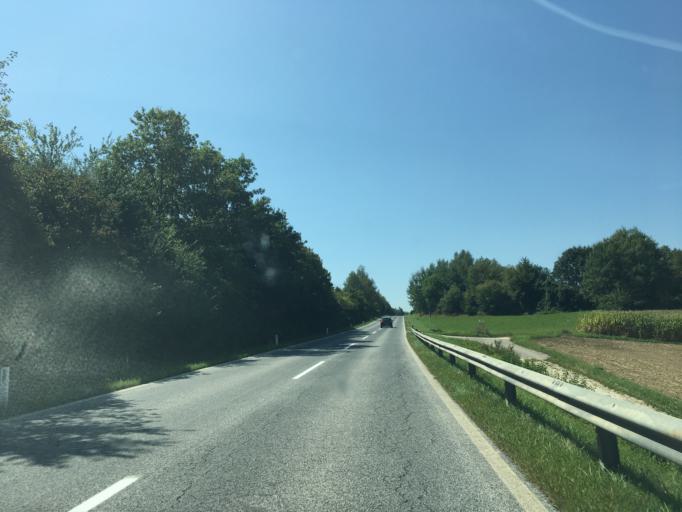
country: AT
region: Carinthia
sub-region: Politischer Bezirk Volkermarkt
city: Griffen
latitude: 46.6874
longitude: 14.6972
